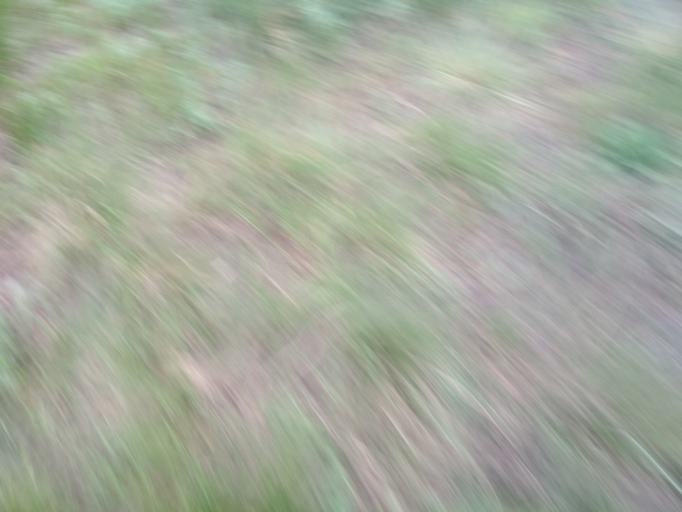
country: RU
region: Rostov
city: Millerovo
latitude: 48.9394
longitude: 40.6755
